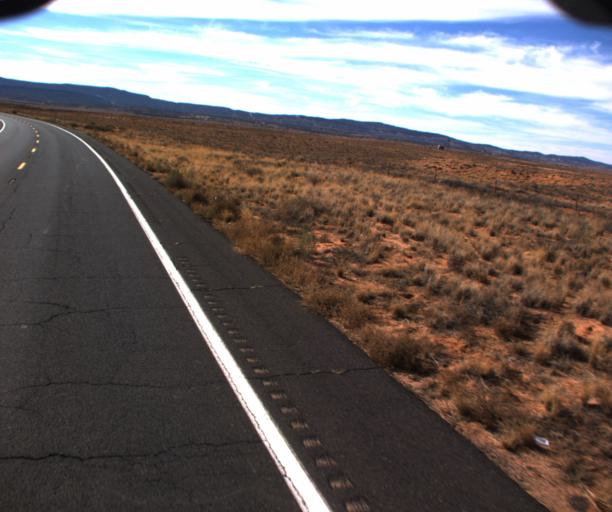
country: US
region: Arizona
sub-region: Coconino County
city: Kaibito
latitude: 36.4860
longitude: -110.7053
